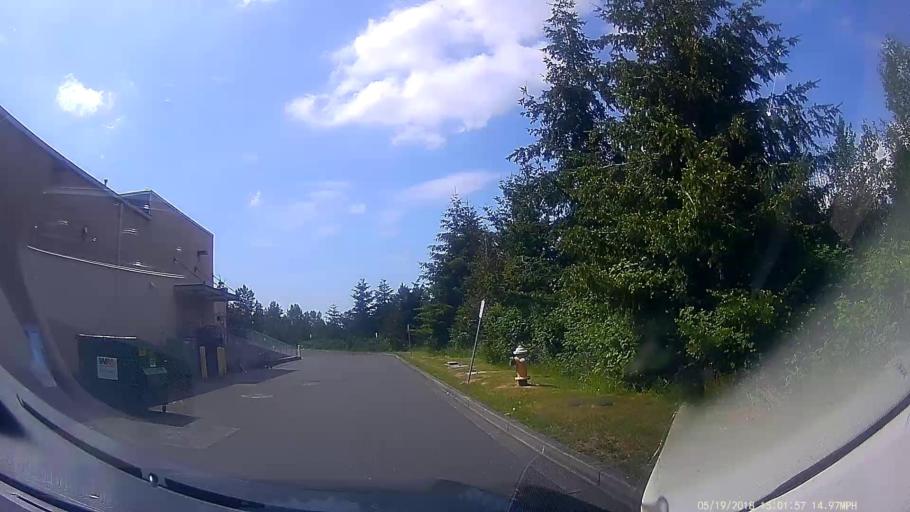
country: US
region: Washington
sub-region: Skagit County
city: Mount Vernon
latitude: 48.4226
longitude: -122.3071
